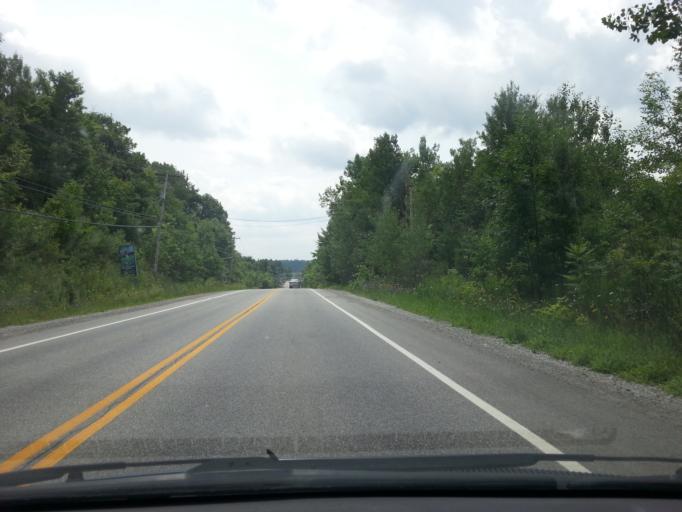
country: CA
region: Quebec
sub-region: Outaouais
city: Gatineau
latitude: 45.5106
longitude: -75.7639
